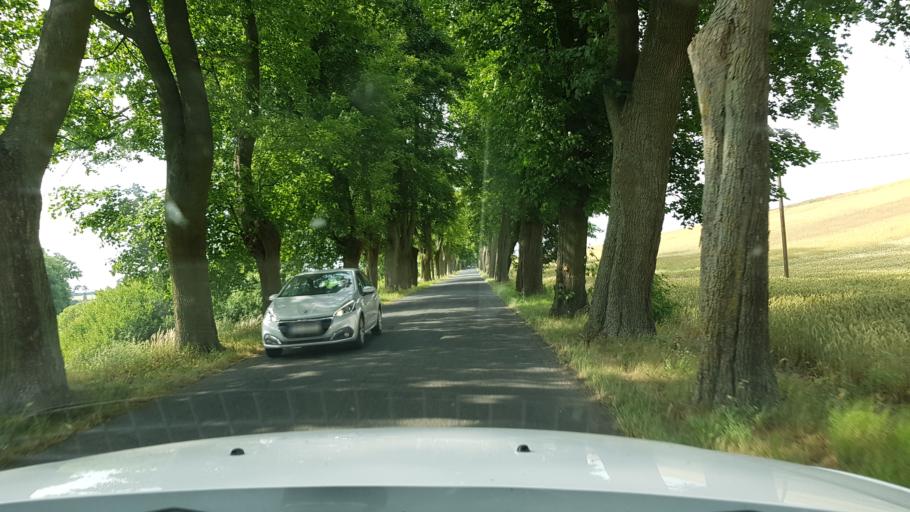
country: PL
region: West Pomeranian Voivodeship
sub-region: Powiat gryfinski
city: Moryn
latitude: 52.9074
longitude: 14.3719
